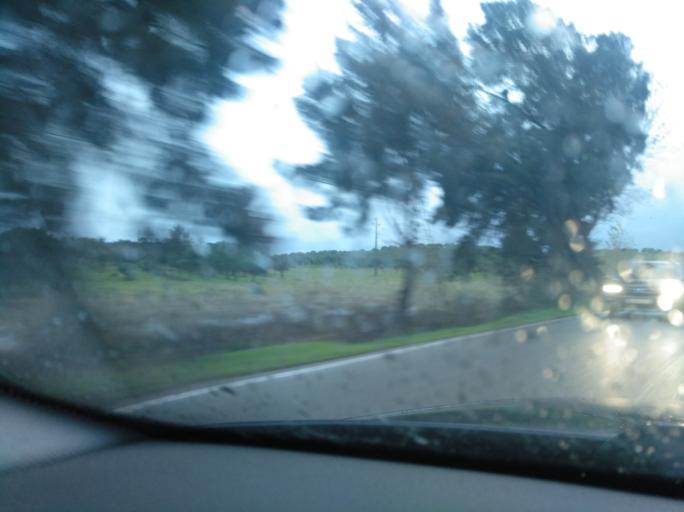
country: PT
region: Faro
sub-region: Castro Marim
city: Castro Marim
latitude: 37.2129
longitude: -7.4710
